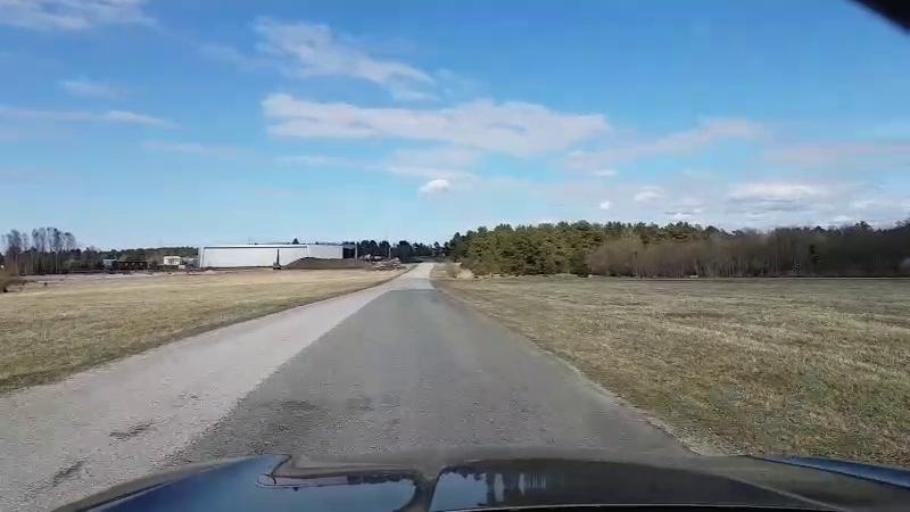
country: EE
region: Harju
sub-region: Saue vald
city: Laagri
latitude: 59.3095
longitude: 24.5991
